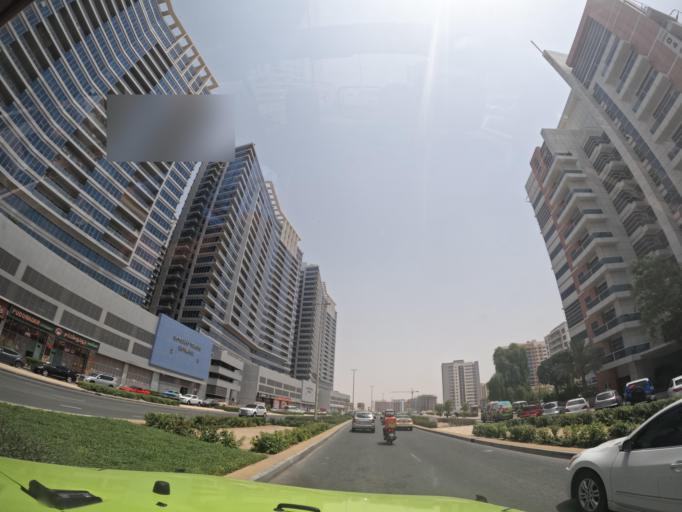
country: AE
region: Dubai
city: Dubai
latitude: 25.0917
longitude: 55.3843
